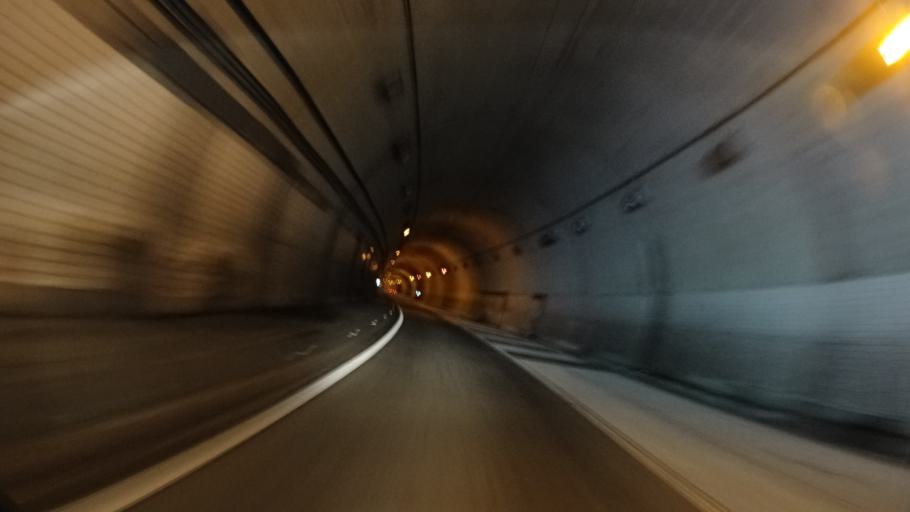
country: JP
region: Ehime
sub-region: Nishiuwa-gun
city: Ikata-cho
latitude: 33.3949
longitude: 132.1524
